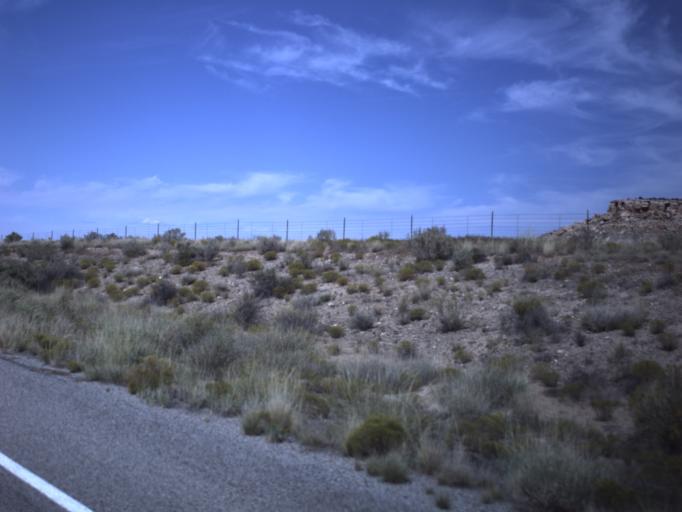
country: US
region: Colorado
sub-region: Montezuma County
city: Towaoc
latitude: 37.1556
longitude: -109.0535
